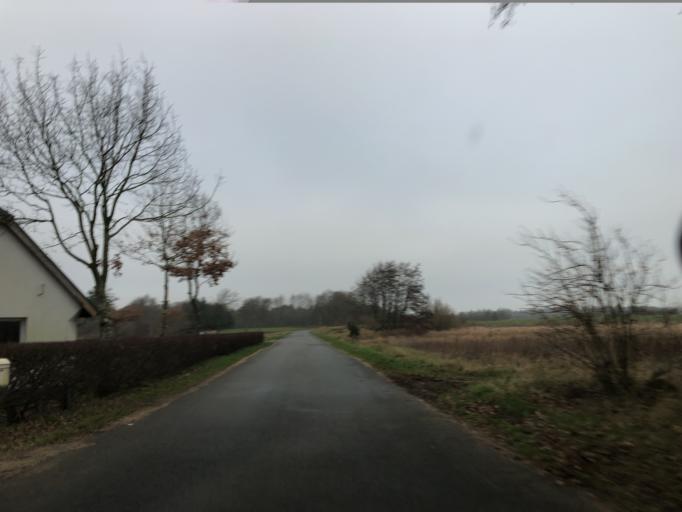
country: DK
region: Central Jutland
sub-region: Holstebro Kommune
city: Ulfborg
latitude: 56.2015
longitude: 8.3140
